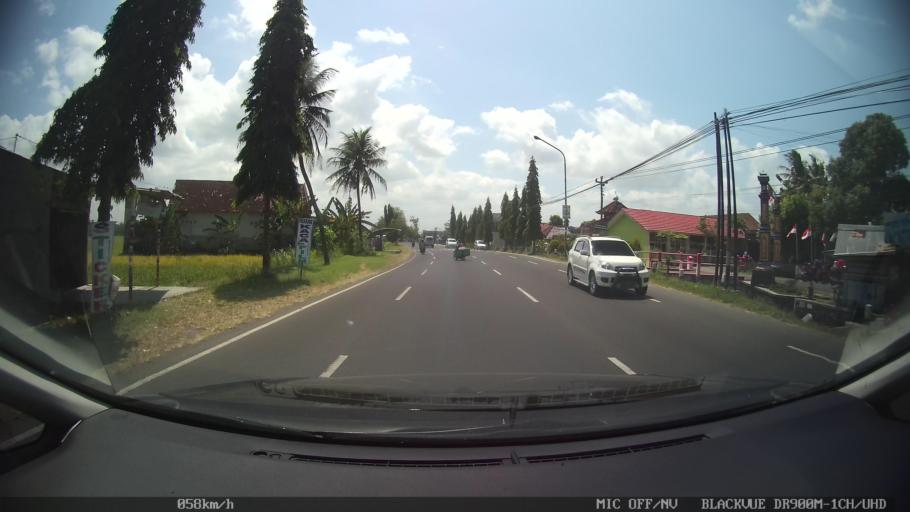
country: ID
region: Daerah Istimewa Yogyakarta
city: Pandak
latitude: -7.9250
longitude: 110.2789
